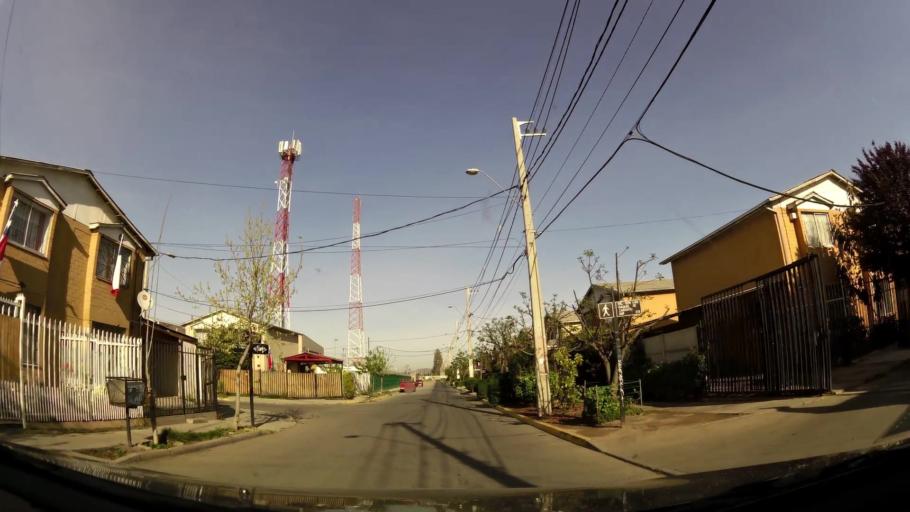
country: CL
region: Santiago Metropolitan
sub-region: Provincia de Cordillera
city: Puente Alto
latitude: -33.6128
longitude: -70.5969
